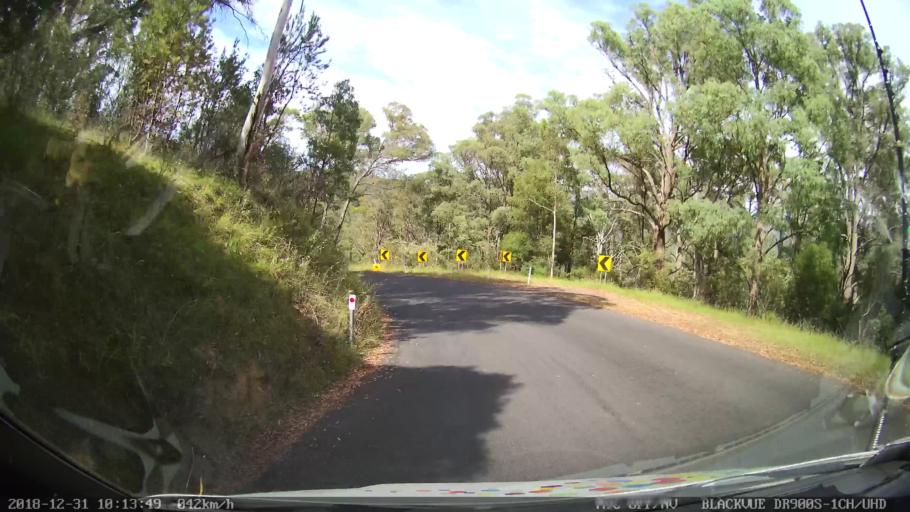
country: AU
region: New South Wales
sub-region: Snowy River
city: Jindabyne
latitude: -36.5394
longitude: 148.1523
